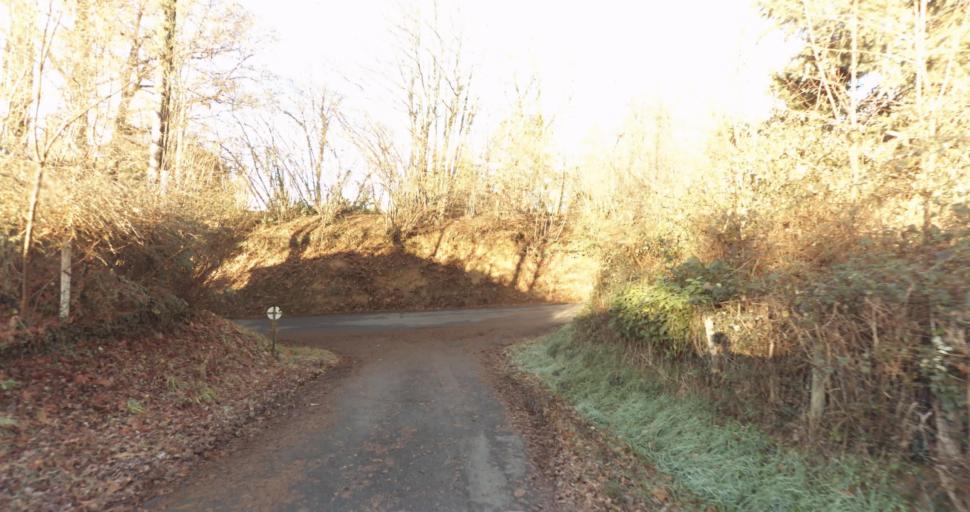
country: FR
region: Limousin
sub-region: Departement de la Haute-Vienne
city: Aixe-sur-Vienne
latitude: 45.8136
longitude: 1.1505
